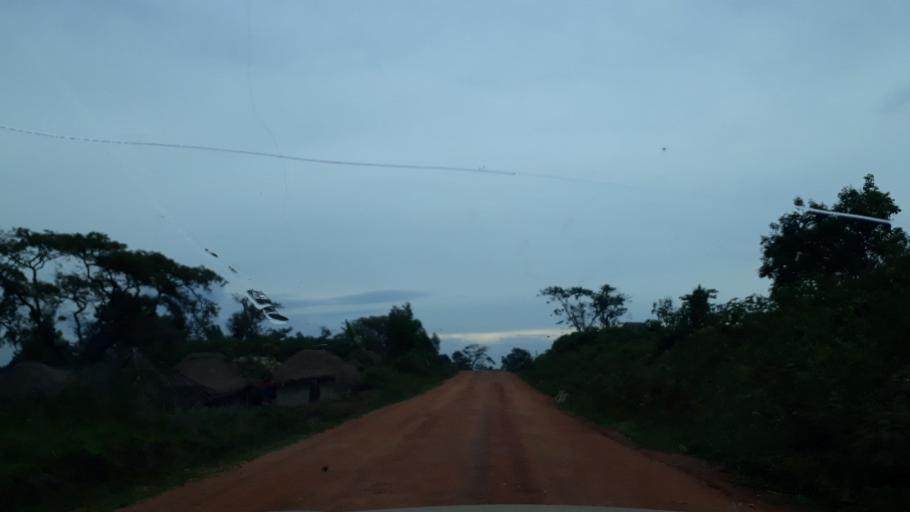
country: UG
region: Northern Region
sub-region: Zombo District
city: Paidha
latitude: 2.2039
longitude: 30.7495
